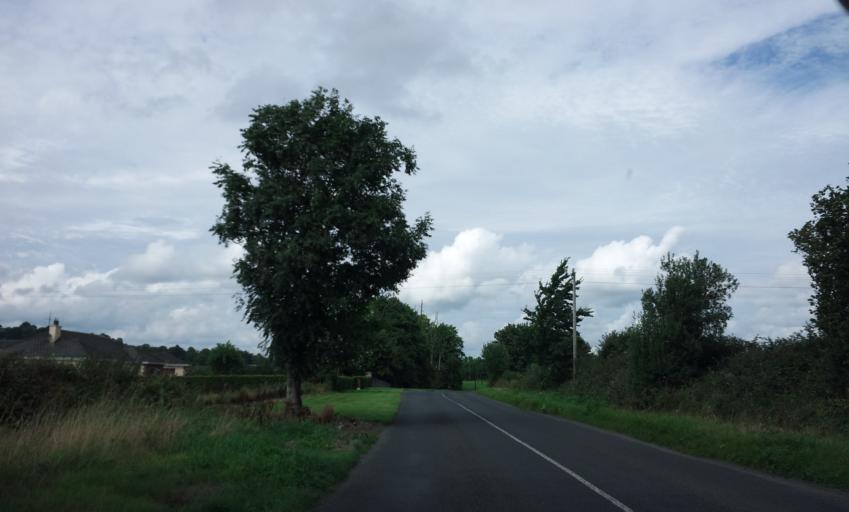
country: IE
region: Leinster
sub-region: Laois
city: Stradbally
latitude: 53.0022
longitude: -7.2248
